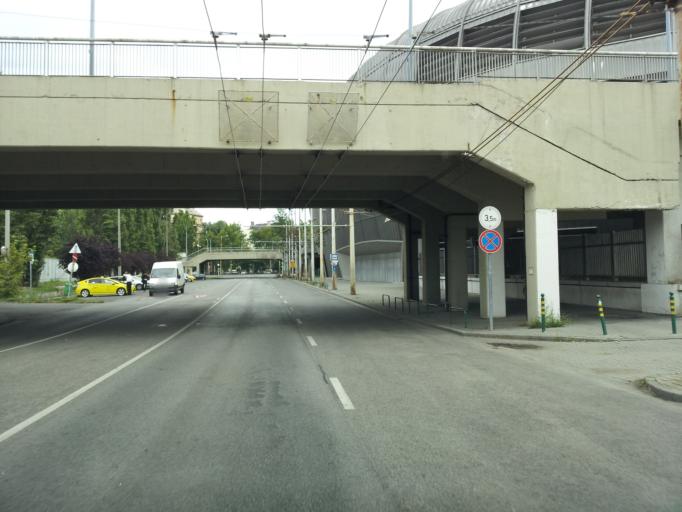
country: HU
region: Budapest
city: Budapest XIV. keruelet
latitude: 47.5014
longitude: 19.1039
